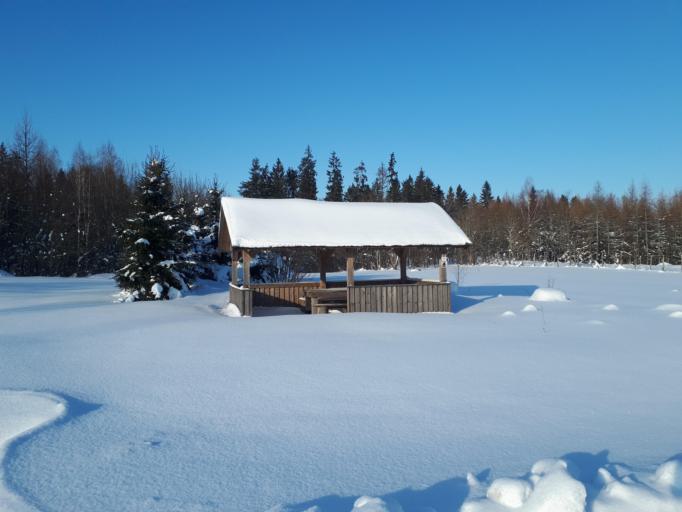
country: LT
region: Alytaus apskritis
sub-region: Alytaus rajonas
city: Daugai
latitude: 54.4331
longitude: 24.2775
